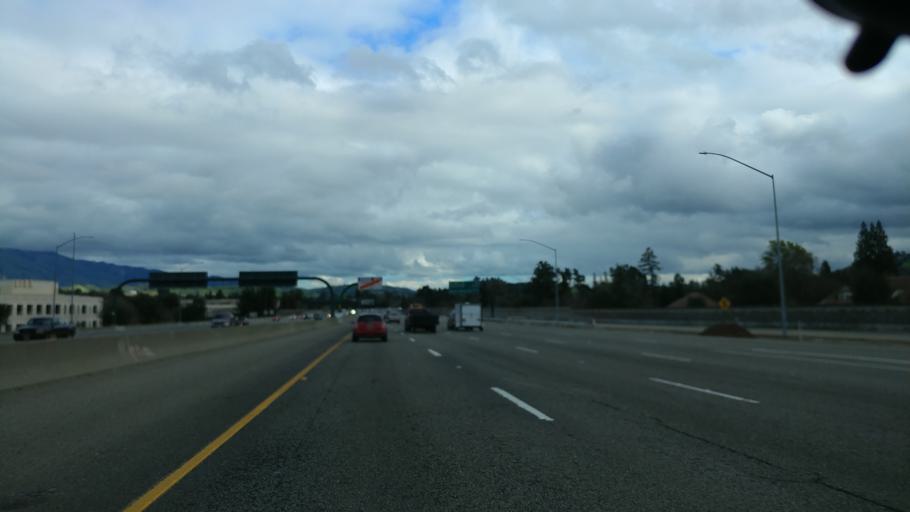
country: US
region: California
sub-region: Contra Costa County
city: Walnut Creek
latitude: 37.8933
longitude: -122.0659
